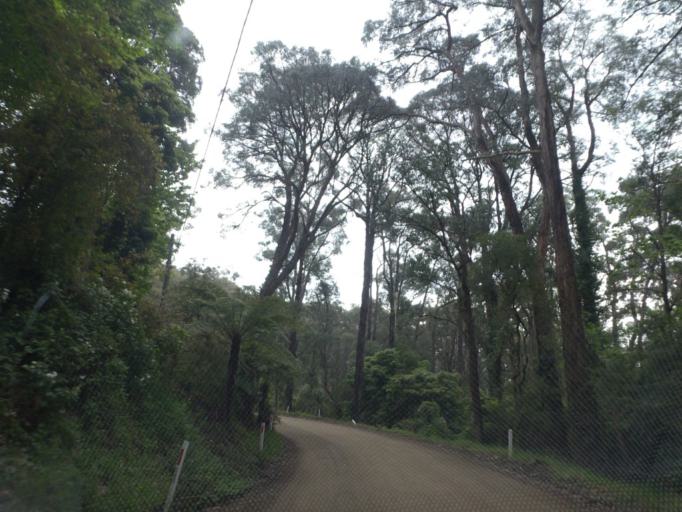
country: AU
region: Victoria
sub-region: Yarra Ranges
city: Olinda
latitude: -37.8569
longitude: 145.3425
